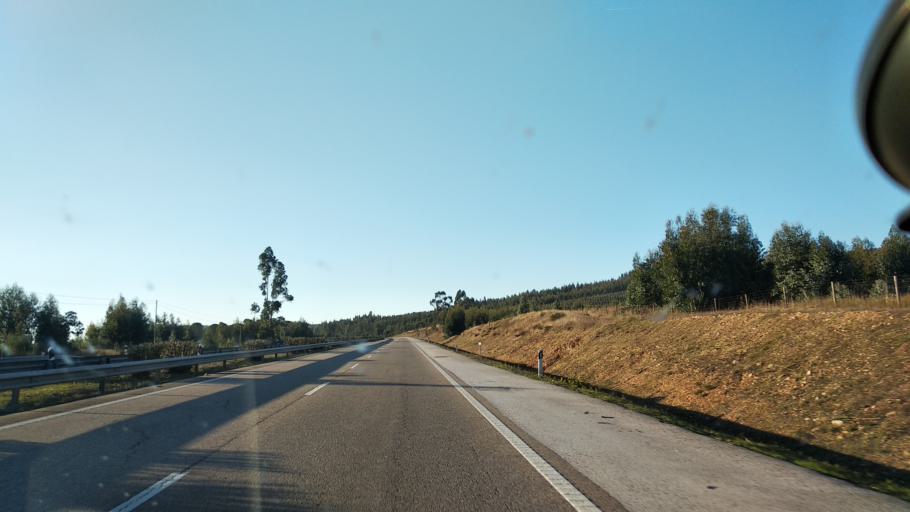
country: PT
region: Santarem
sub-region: Constancia
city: Constancia
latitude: 39.4902
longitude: -8.2930
